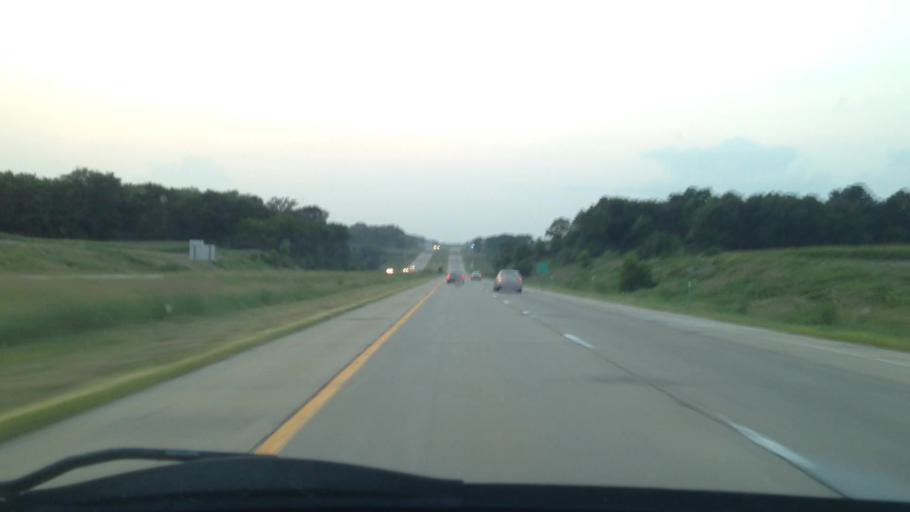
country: US
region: Iowa
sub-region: Benton County
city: Urbana
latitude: 42.3154
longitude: -91.9815
